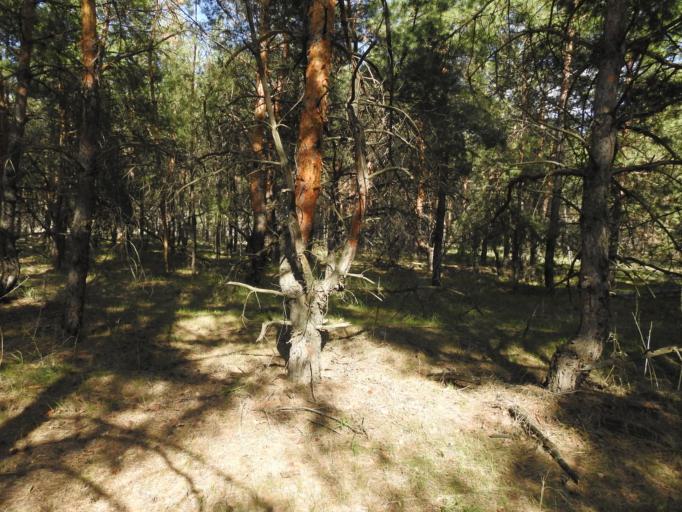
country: RU
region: Saratov
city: Krasnyy Yar
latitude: 51.5891
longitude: 46.5429
